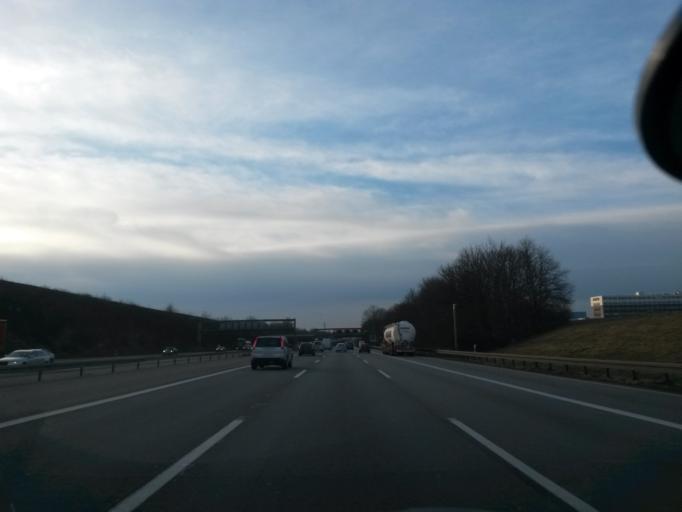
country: DE
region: Bavaria
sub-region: Upper Bavaria
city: Kirchheim bei Muenchen
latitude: 48.1592
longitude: 11.7477
